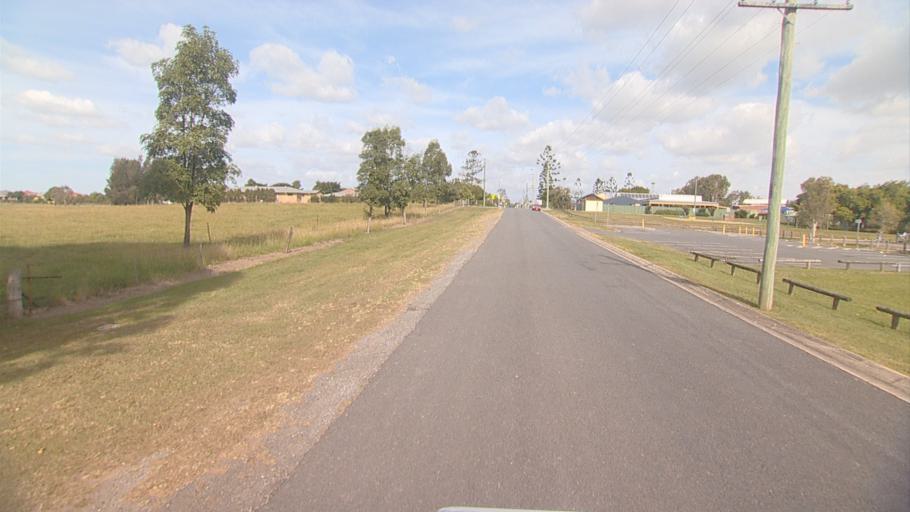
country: AU
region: Queensland
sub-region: Logan
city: Waterford West
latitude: -27.6849
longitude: 153.1580
